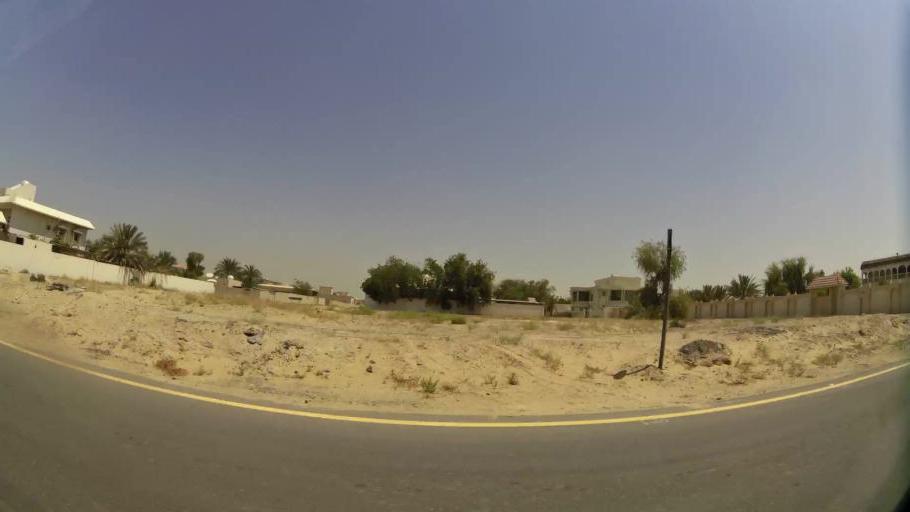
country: AE
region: Ajman
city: Ajman
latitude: 25.3994
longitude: 55.5151
